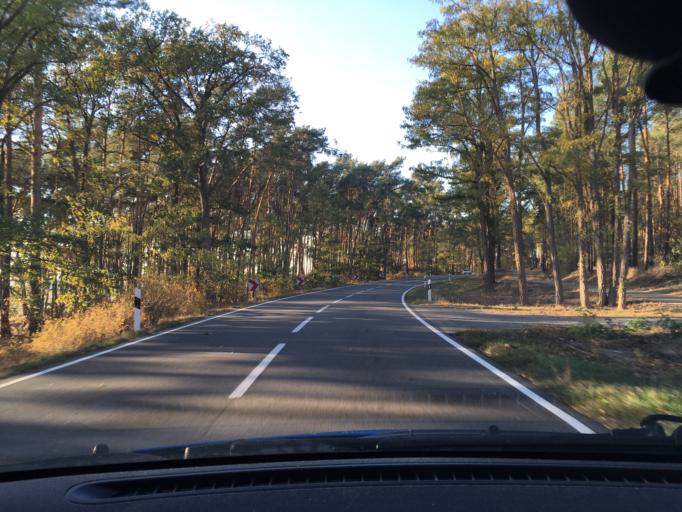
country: DE
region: Lower Saxony
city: Neu Darchau
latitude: 53.2726
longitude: 10.9424
